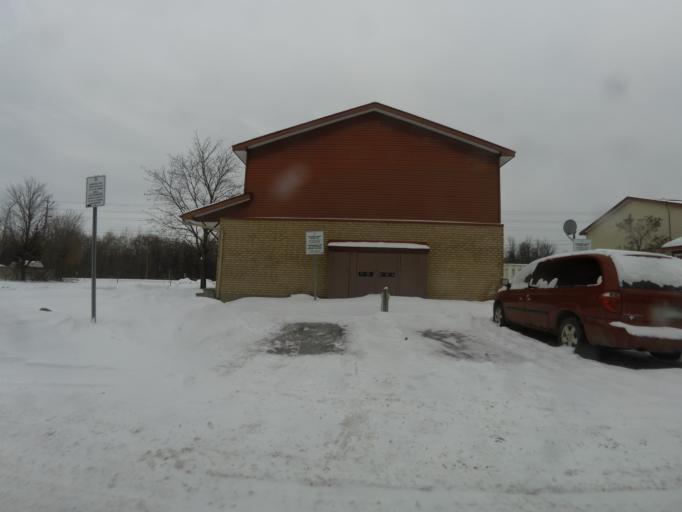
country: CA
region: Ontario
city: Ottawa
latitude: 45.3701
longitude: -75.6091
